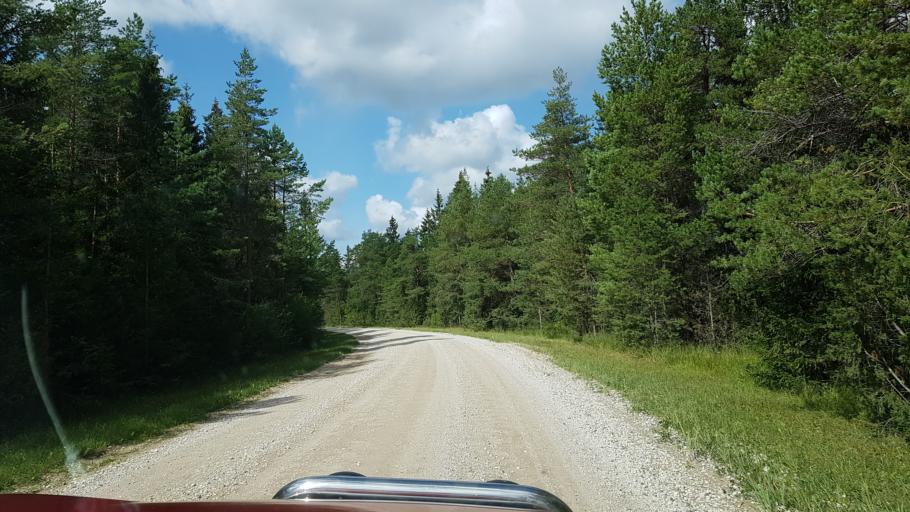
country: EE
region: Raplamaa
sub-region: Rapla vald
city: Rapla
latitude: 58.9578
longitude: 24.6543
